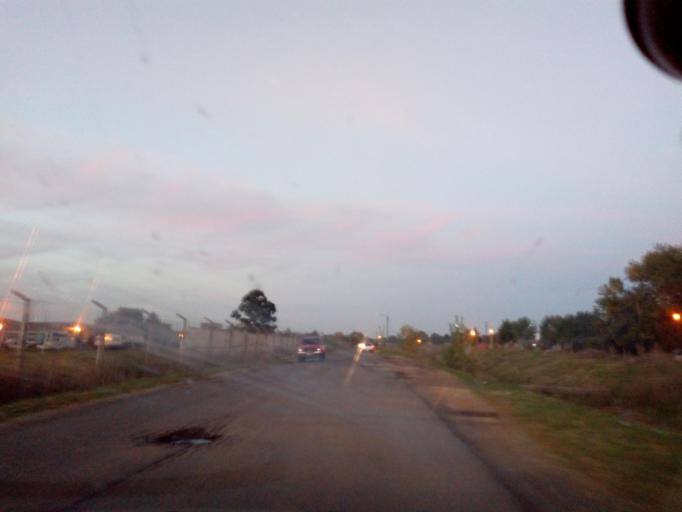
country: AR
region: Buenos Aires
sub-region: Partido de La Plata
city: La Plata
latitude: -34.9968
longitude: -58.0376
